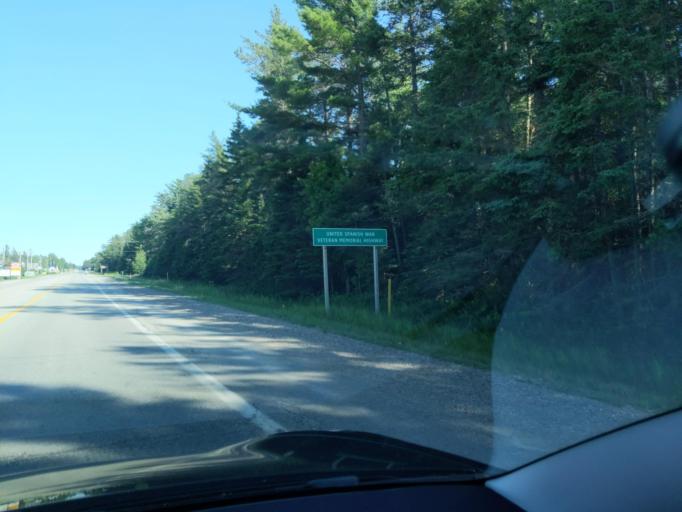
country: US
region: Michigan
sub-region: Mackinac County
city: Saint Ignace
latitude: 45.7660
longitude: -84.7224
